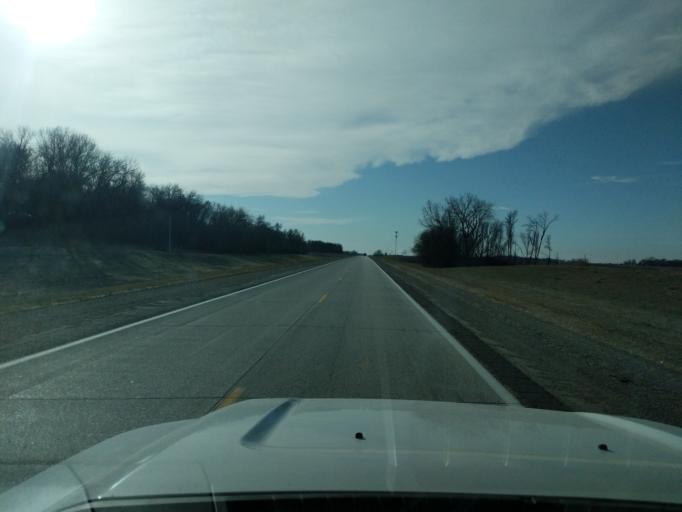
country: US
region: Minnesota
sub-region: Yellow Medicine County
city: Granite Falls
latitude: 44.8526
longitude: -95.4836
